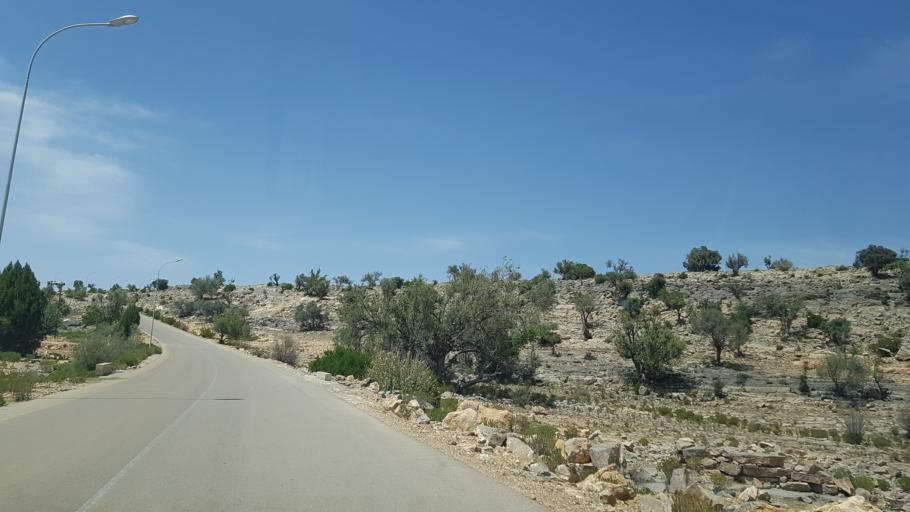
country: OM
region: Al Batinah
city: Bayt al `Awabi
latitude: 23.1220
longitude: 57.6026
